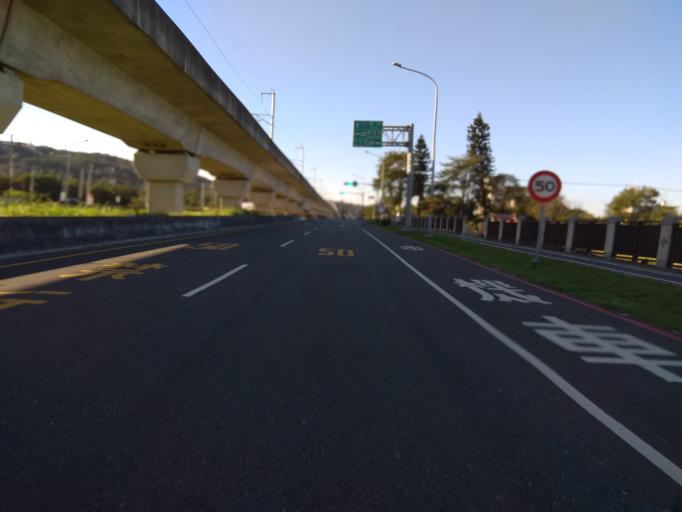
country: TW
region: Taiwan
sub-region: Hsinchu
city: Zhubei
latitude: 24.8862
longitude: 121.0720
